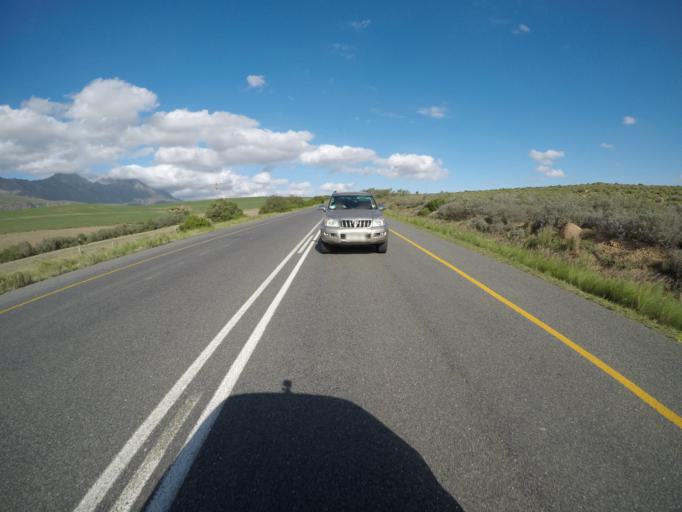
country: ZA
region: Western Cape
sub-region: Cape Winelands District Municipality
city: Ashton
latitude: -33.9510
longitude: 20.2275
